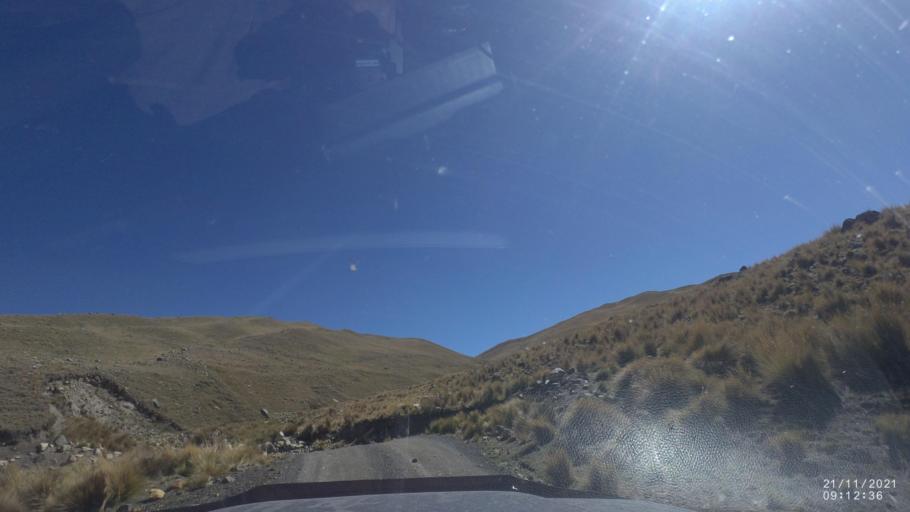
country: BO
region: Cochabamba
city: Cochabamba
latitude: -17.1427
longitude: -66.2558
